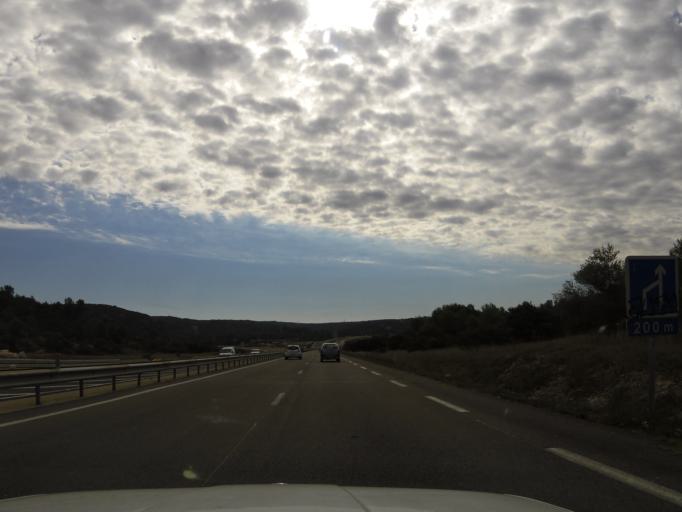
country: FR
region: Languedoc-Roussillon
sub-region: Departement du Gard
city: La Calmette
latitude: 43.9060
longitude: 4.2754
